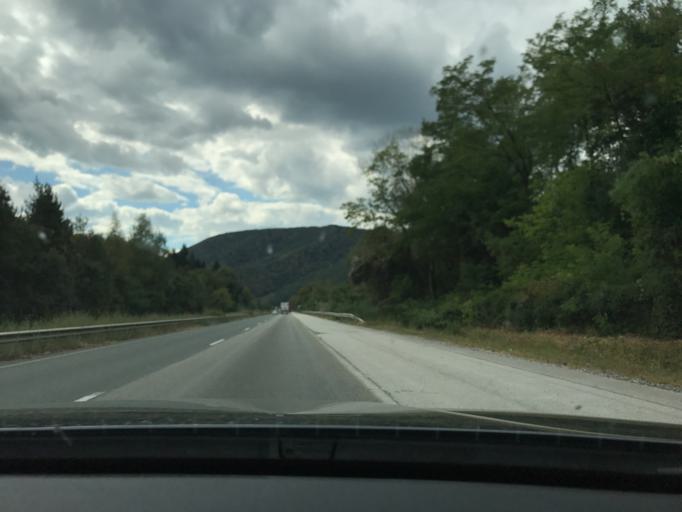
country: BG
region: Sofiya
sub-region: Obshtina Botevgrad
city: Botevgrad
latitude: 42.8844
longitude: 23.8131
